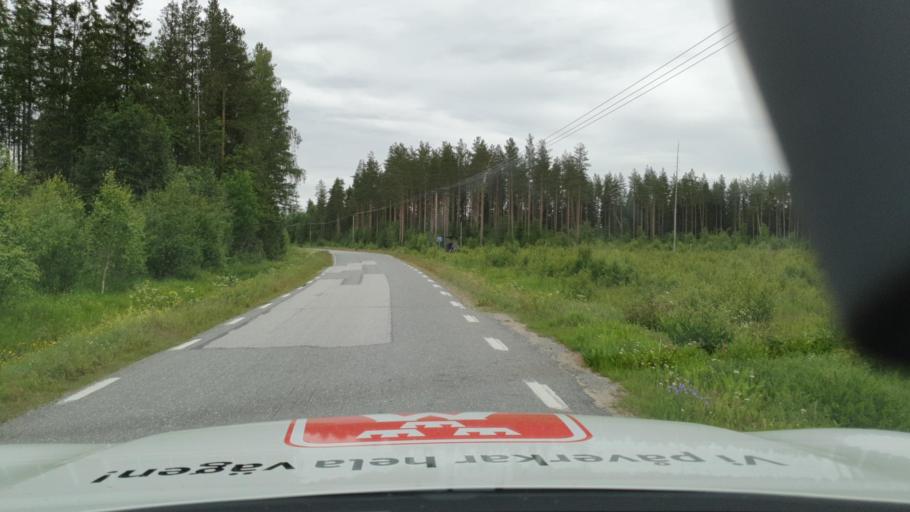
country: SE
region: Vaesterbotten
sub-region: Nordmalings Kommun
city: Nordmaling
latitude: 63.5176
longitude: 19.4215
